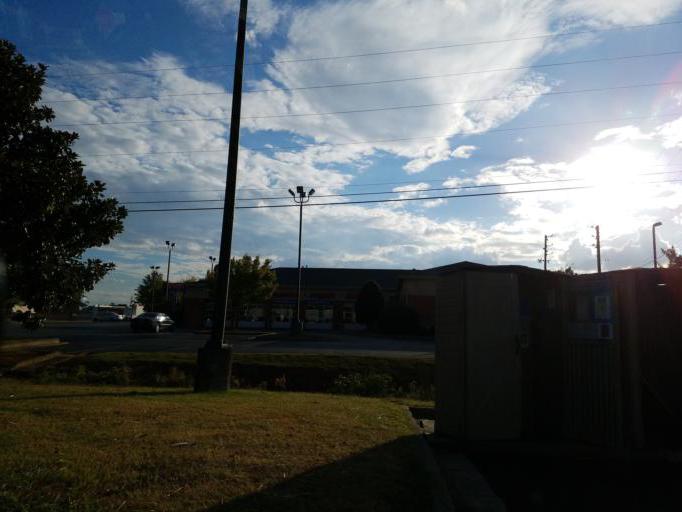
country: US
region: Georgia
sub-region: Bartow County
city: Cartersville
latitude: 34.1998
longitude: -84.7903
